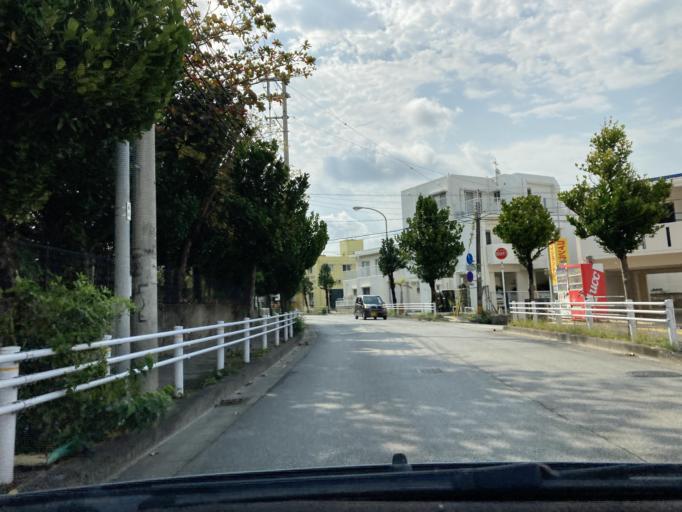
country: JP
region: Okinawa
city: Tomigusuku
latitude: 26.1997
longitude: 127.7178
